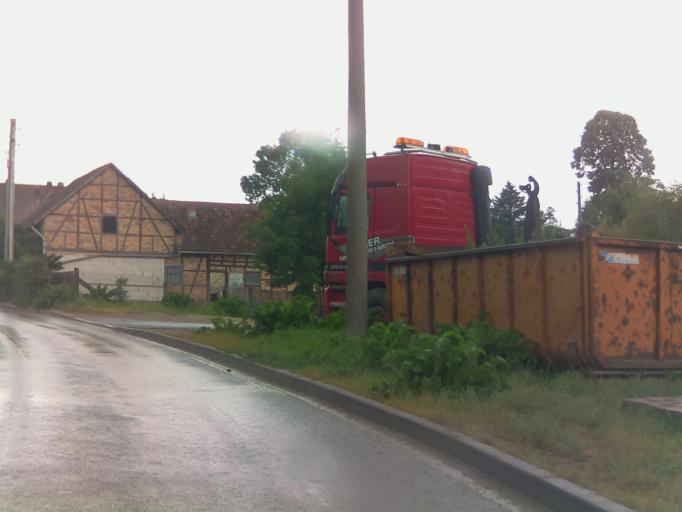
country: DE
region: Thuringia
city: Stadtilm
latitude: 50.7448
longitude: 11.0820
